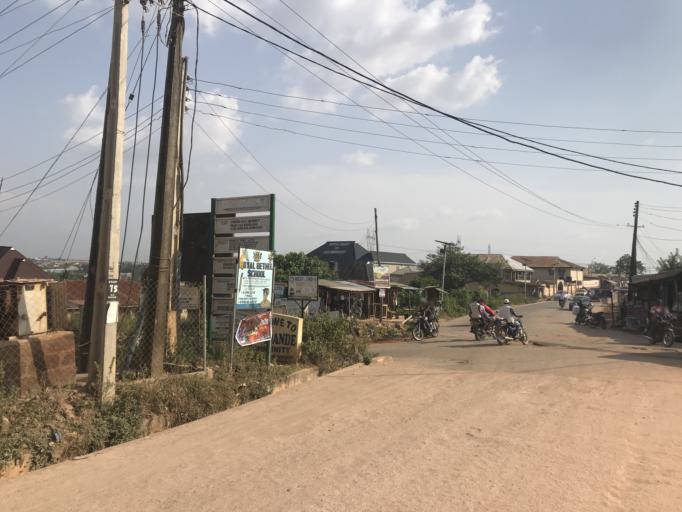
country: NG
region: Osun
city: Osogbo
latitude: 7.8041
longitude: 4.5560
